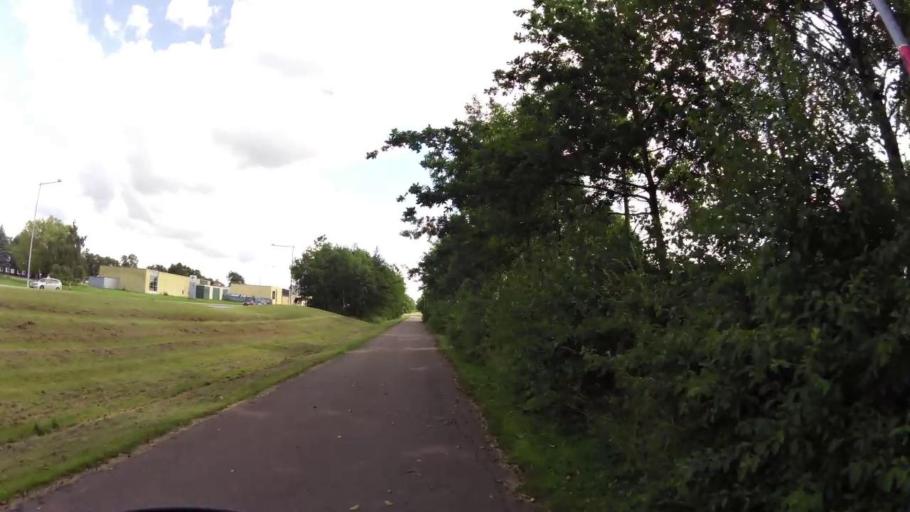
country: SE
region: OEstergoetland
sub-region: Linkopings Kommun
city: Linkoping
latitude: 58.4287
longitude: 15.6048
